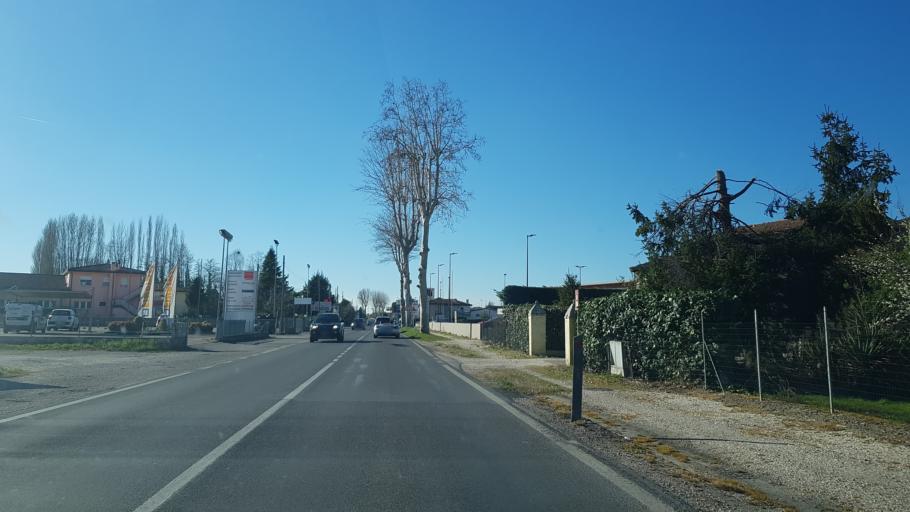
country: IT
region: Veneto
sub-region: Provincia di Rovigo
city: Villadose
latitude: 45.0684
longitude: 11.8905
